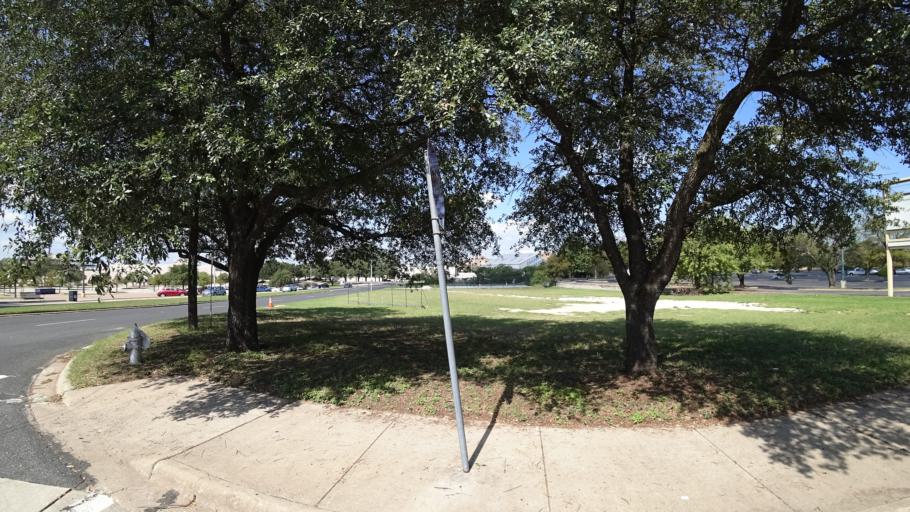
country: US
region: Texas
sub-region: Travis County
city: Austin
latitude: 30.3264
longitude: -97.7083
